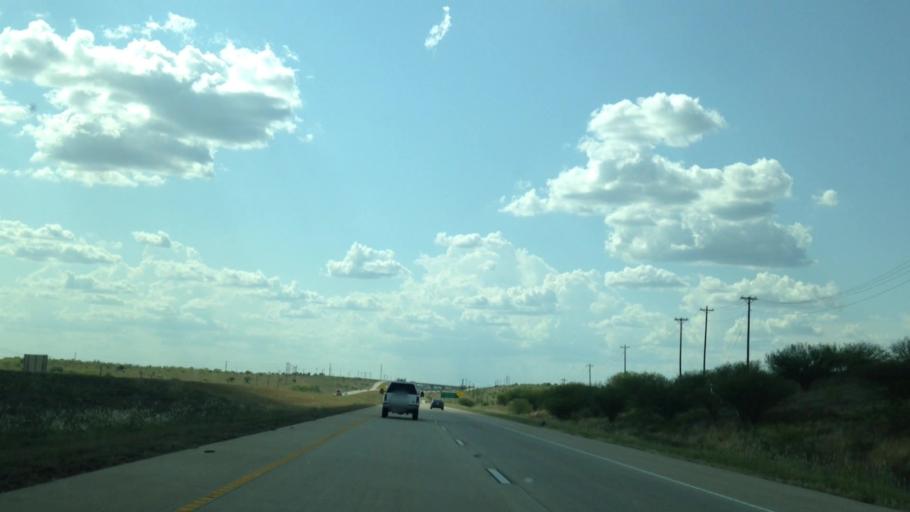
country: US
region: Texas
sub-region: Travis County
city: Onion Creek
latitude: 30.0961
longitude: -97.7657
